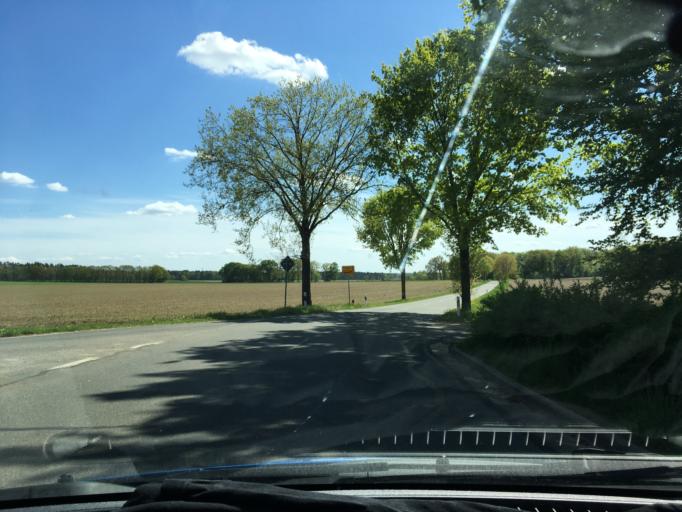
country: DE
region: Lower Saxony
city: Zernien
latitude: 53.0324
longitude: 10.8880
